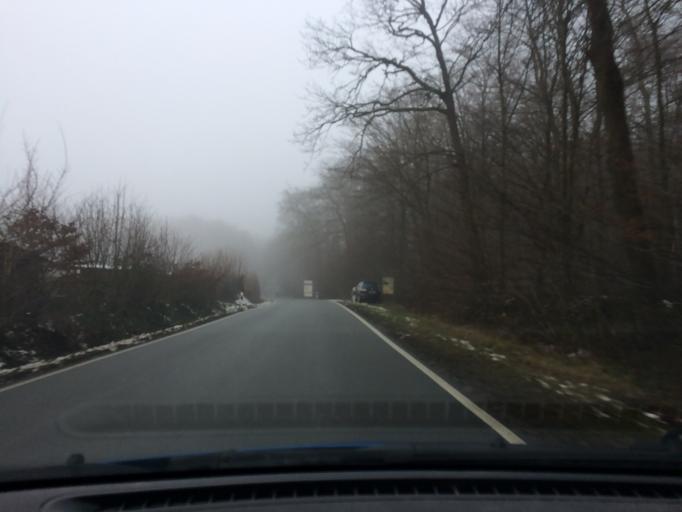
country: DE
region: Schleswig-Holstein
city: Schwarzenbek
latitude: 53.4942
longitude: 10.4716
